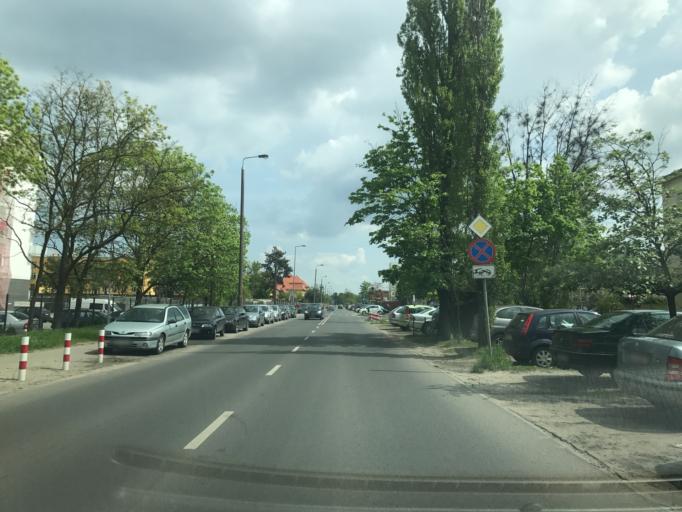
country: PL
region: Kujawsko-Pomorskie
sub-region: Bydgoszcz
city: Bydgoszcz
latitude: 53.1436
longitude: 18.0104
